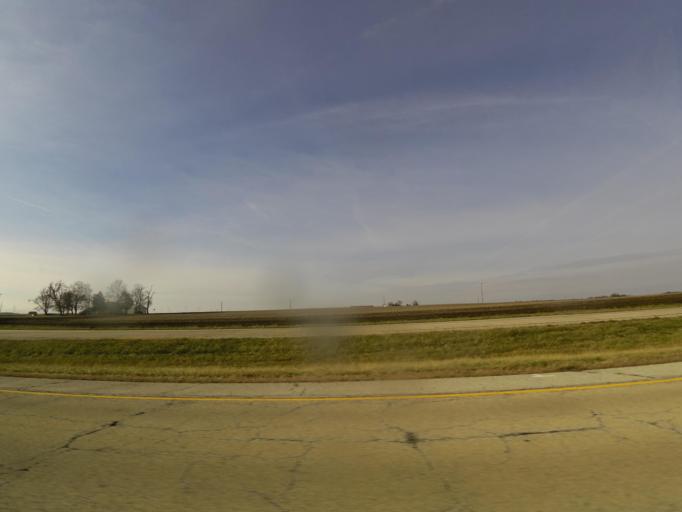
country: US
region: Illinois
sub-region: Macon County
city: Maroa
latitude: 40.0748
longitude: -88.9656
